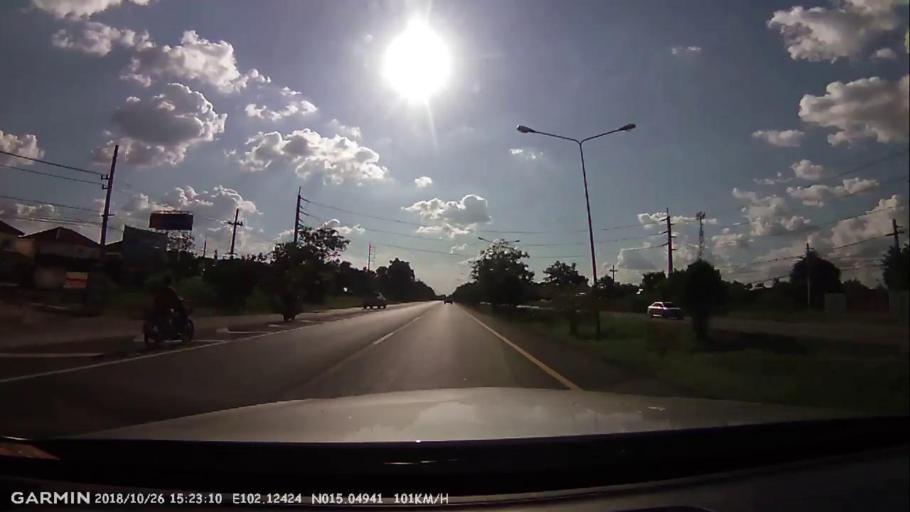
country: TH
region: Nakhon Ratchasima
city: Nakhon Ratchasima
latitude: 15.0494
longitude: 102.1243
